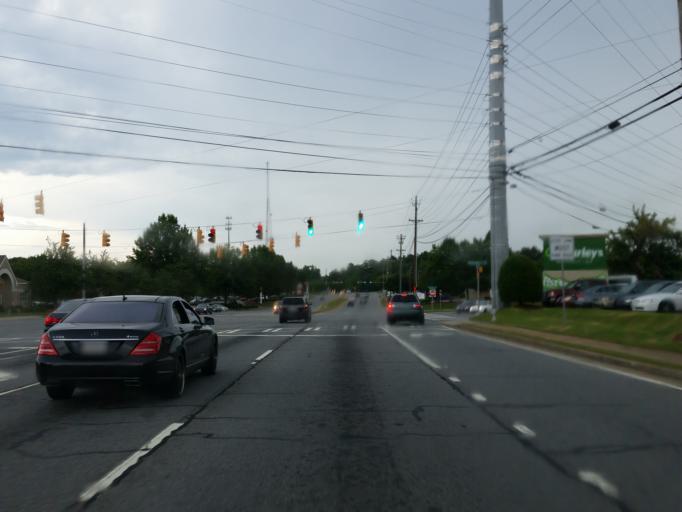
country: US
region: Georgia
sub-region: Cherokee County
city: Woodstock
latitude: 34.0359
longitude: -84.4630
